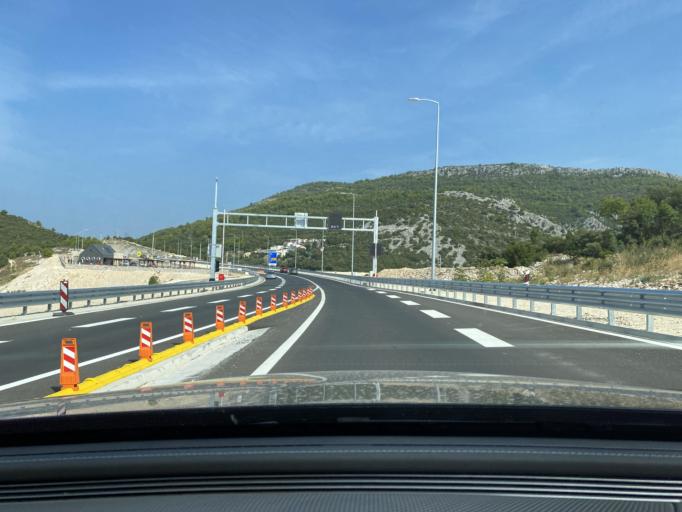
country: BA
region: Federation of Bosnia and Herzegovina
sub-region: Hercegovacko-Bosanski Kanton
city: Neum
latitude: 42.9428
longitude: 17.5423
